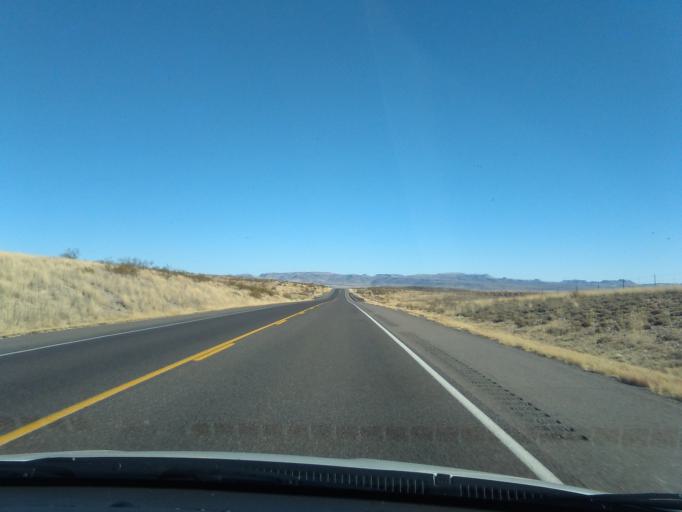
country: US
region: New Mexico
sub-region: Dona Ana County
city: Hatch
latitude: 32.5773
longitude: -107.4387
